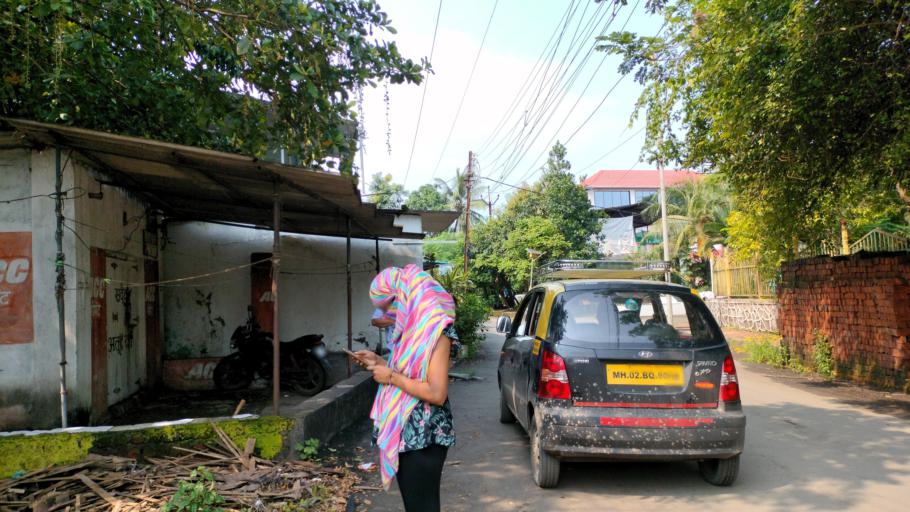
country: IN
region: Maharashtra
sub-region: Thane
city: Virar
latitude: 19.4281
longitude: 72.7893
